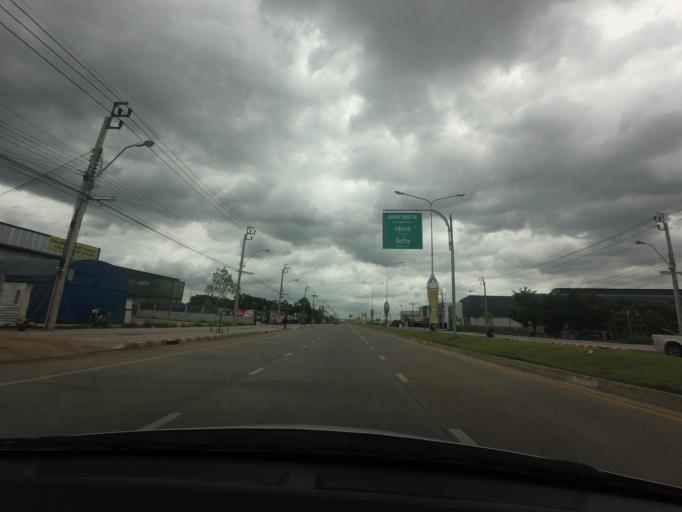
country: TH
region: Bangkok
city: Saphan Sung
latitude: 13.7541
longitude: 100.7152
